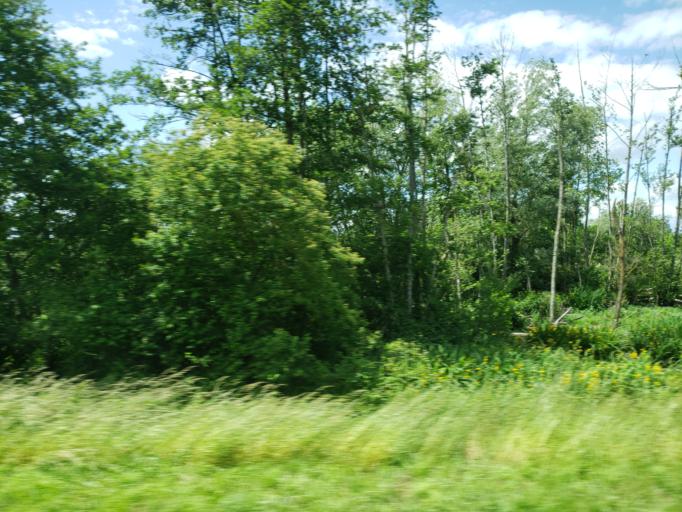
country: FR
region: Bourgogne
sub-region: Departement de l'Yonne
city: Migennes
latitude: 47.9513
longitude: 3.5041
